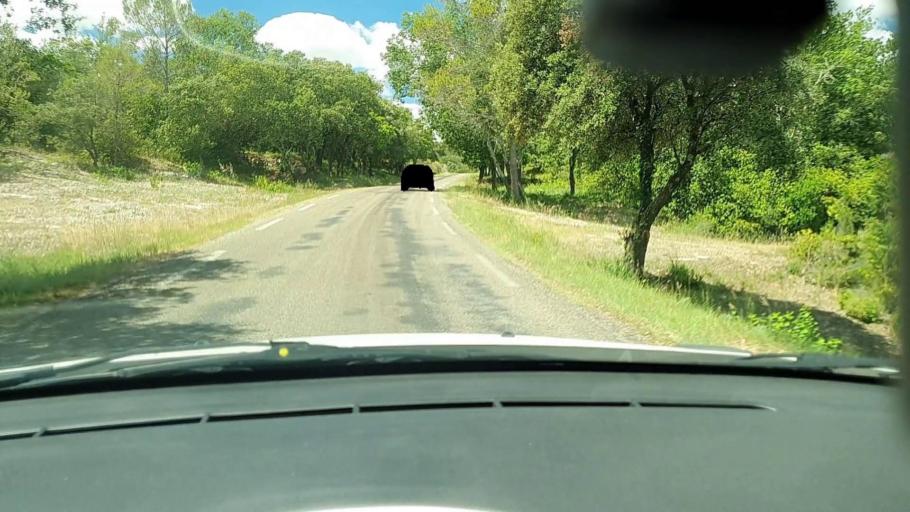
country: FR
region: Languedoc-Roussillon
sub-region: Departement du Gard
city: Cabrieres
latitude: 43.9547
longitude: 4.4512
